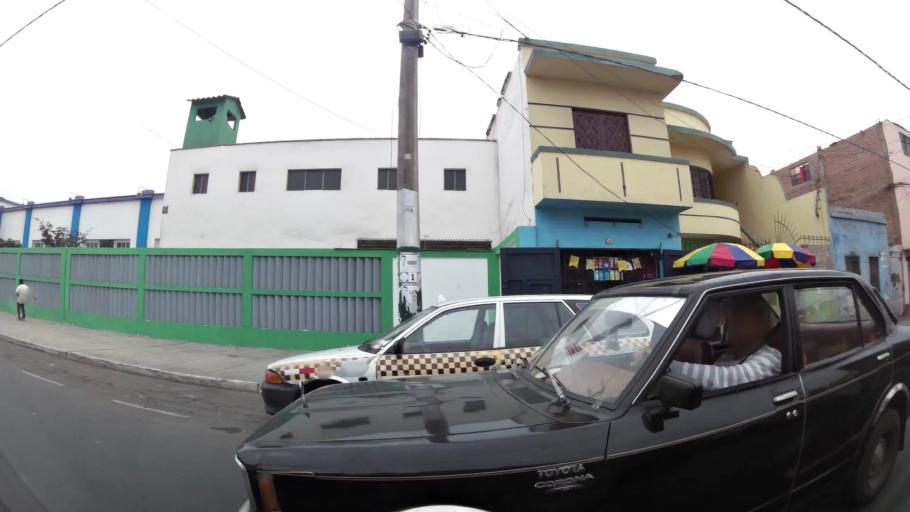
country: PE
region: Callao
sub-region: Callao
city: Callao
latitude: -12.0636
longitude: -77.1336
